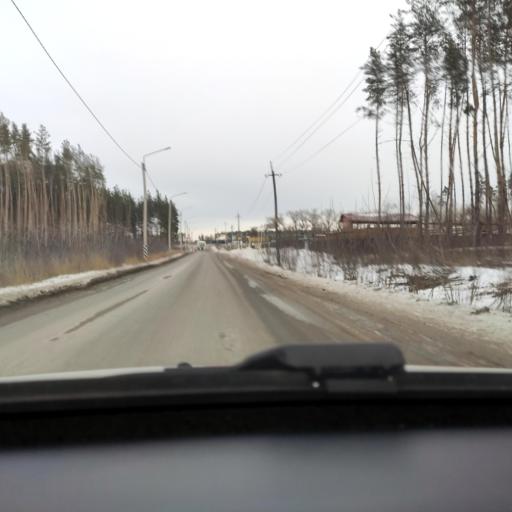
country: RU
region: Voronezj
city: Ramon'
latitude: 51.9377
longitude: 39.2167
